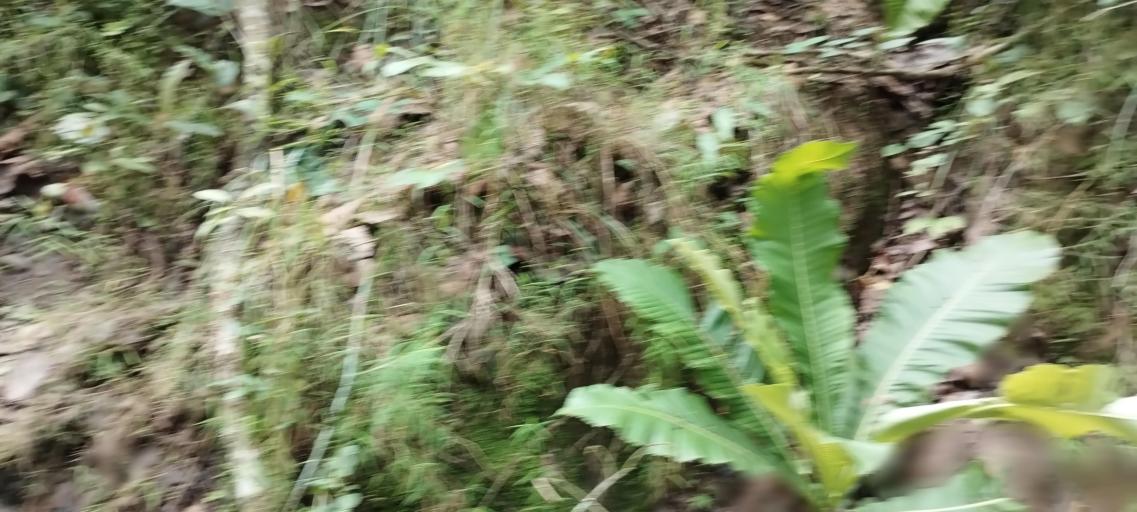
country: NP
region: Far Western
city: Tikapur
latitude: 28.4766
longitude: 81.2524
